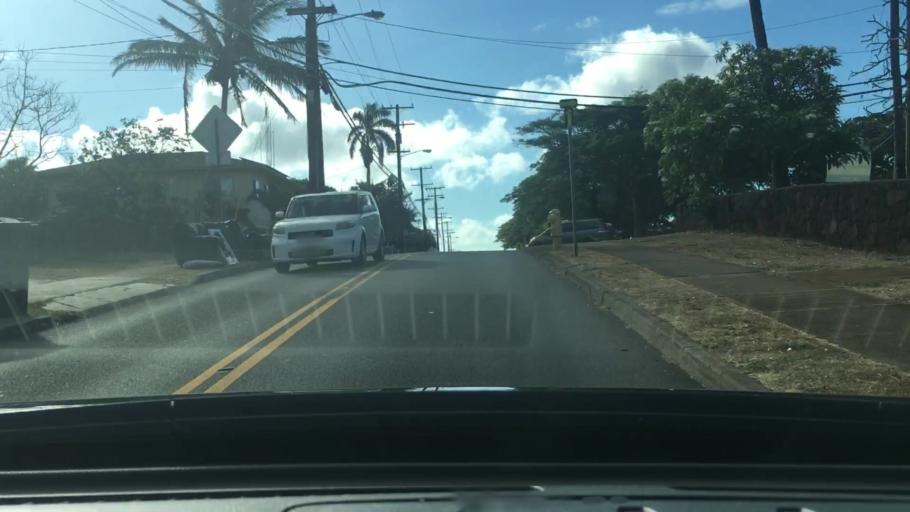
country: US
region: Hawaii
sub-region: Honolulu County
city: Honolulu
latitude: 21.2736
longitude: -157.8011
